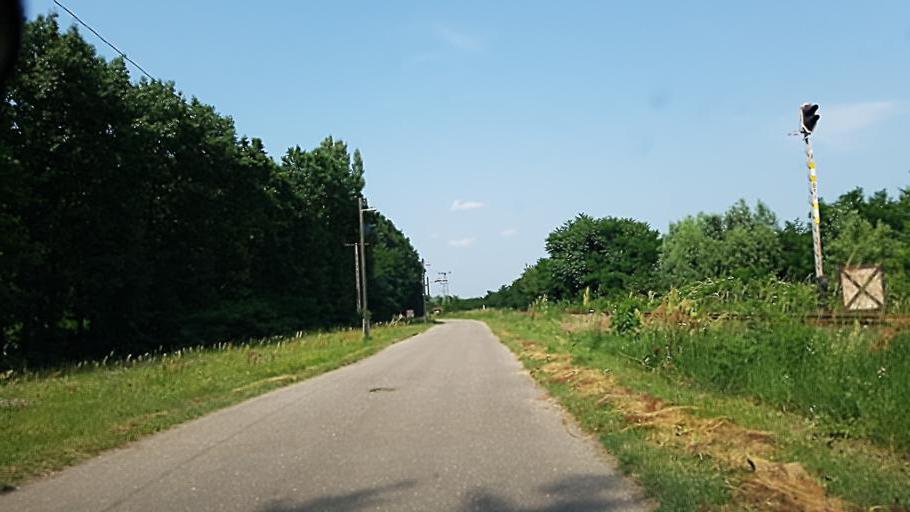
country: HU
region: Jasz-Nagykun-Szolnok
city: Tiszafured
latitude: 47.6222
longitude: 20.7432
